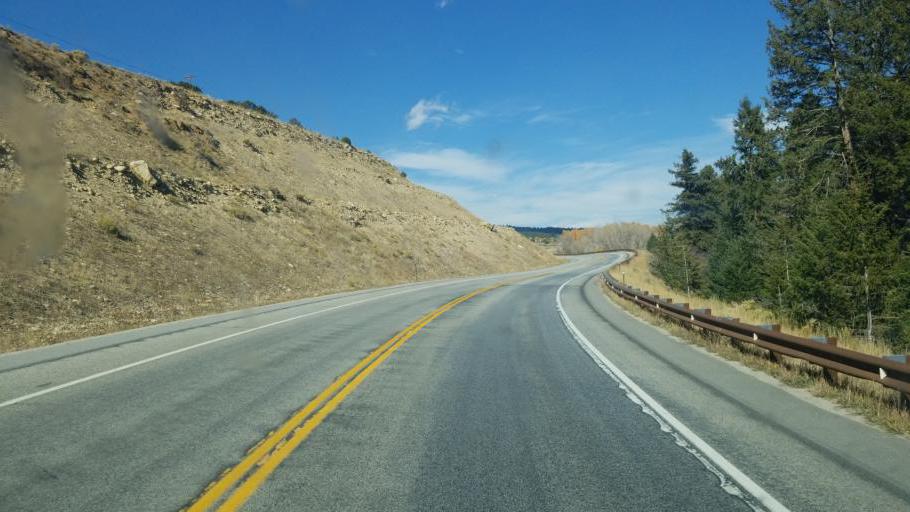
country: US
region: Colorado
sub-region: Chaffee County
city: Buena Vista
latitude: 38.9039
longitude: -106.1752
